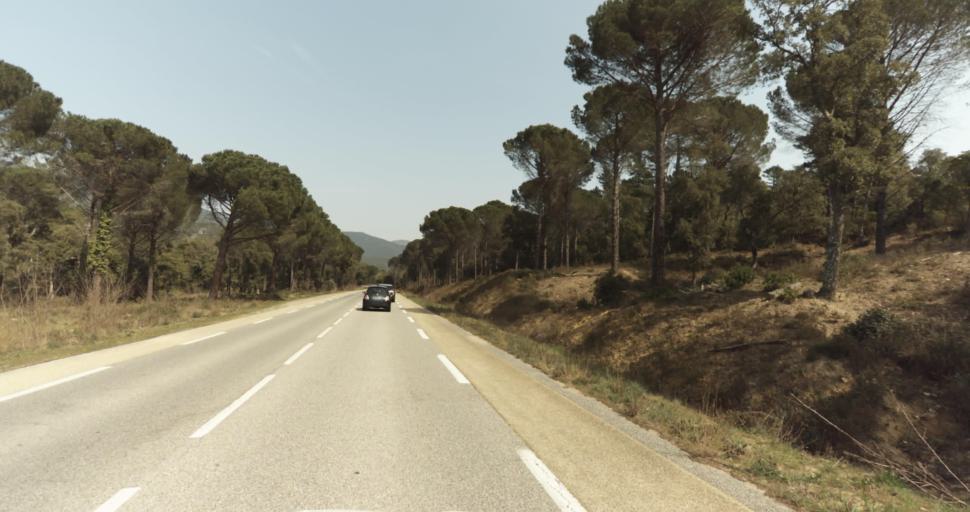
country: FR
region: Provence-Alpes-Cote d'Azur
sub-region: Departement du Var
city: Le Lavandou
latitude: 43.1915
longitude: 6.3753
